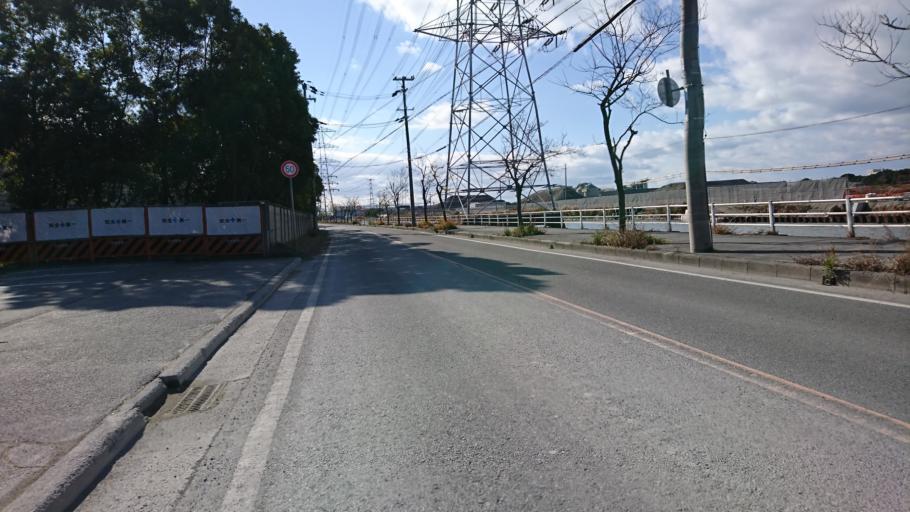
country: JP
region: Hyogo
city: Shirahamacho-usazakiminami
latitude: 34.7662
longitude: 134.7687
